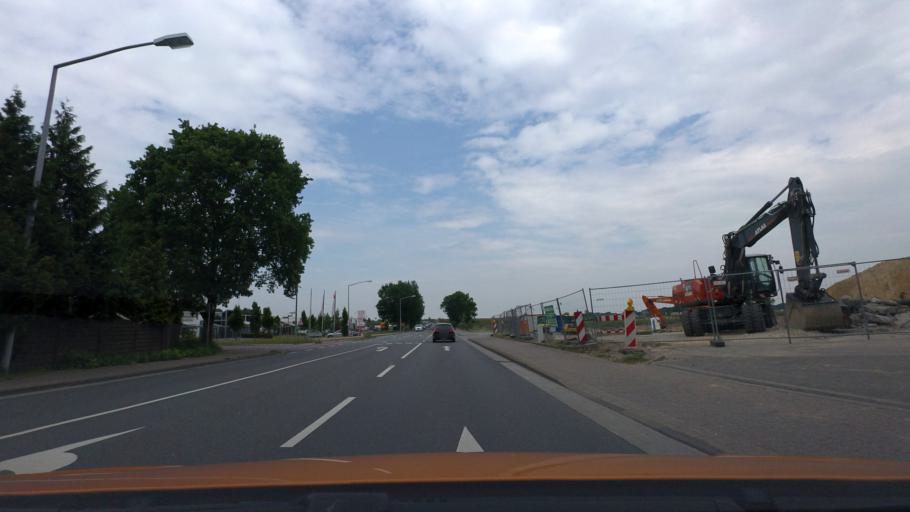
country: DE
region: Lower Saxony
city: Kirchseelte
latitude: 53.0012
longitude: 8.7045
